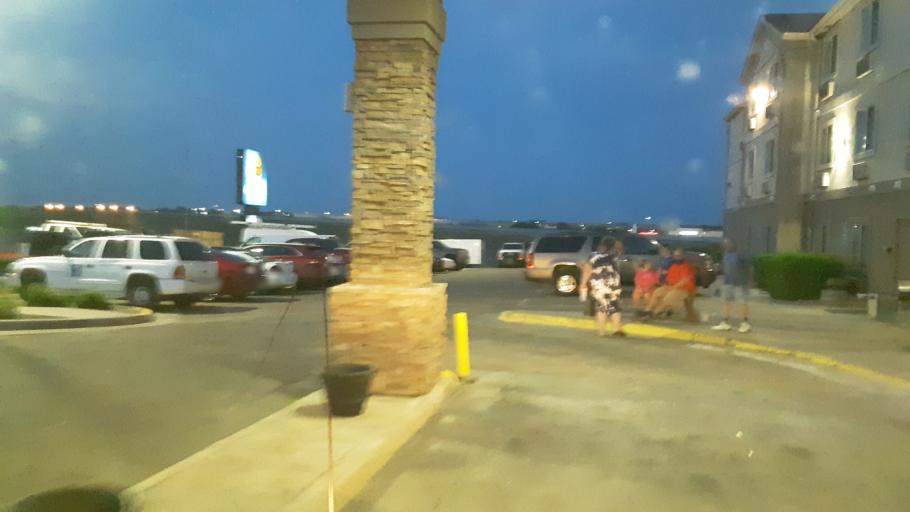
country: US
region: Kansas
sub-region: Finney County
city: Garden City
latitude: 37.9808
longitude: -100.8397
